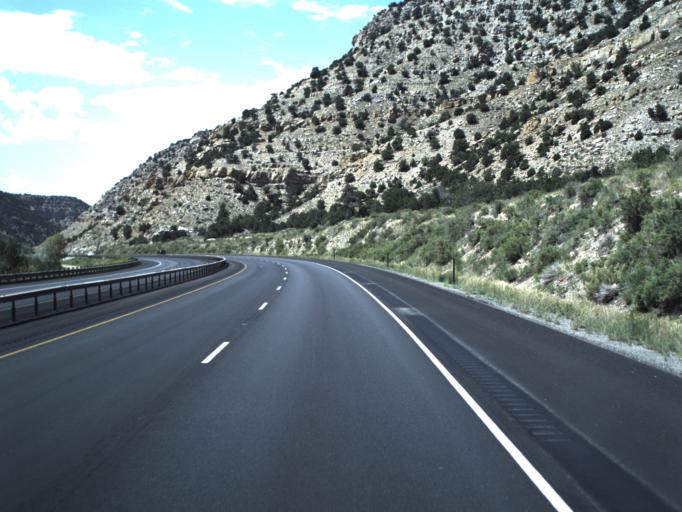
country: US
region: Utah
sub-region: Sevier County
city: Salina
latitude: 38.9023
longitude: -111.6701
